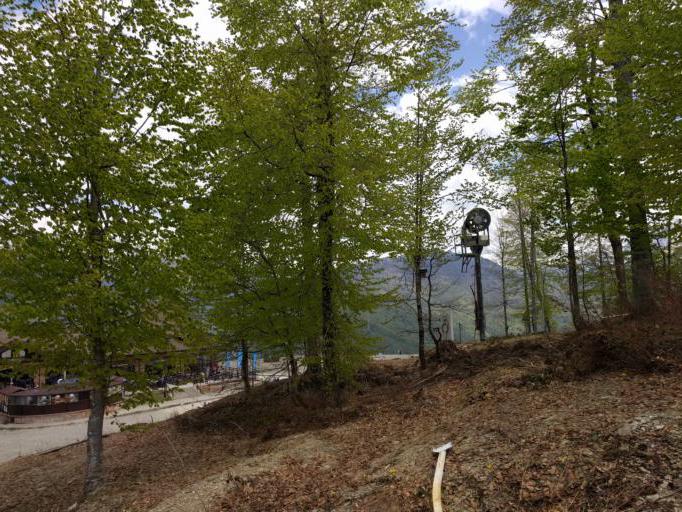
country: RU
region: Krasnodarskiy
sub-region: Sochi City
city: Krasnaya Polyana
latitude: 43.6575
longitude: 40.3191
